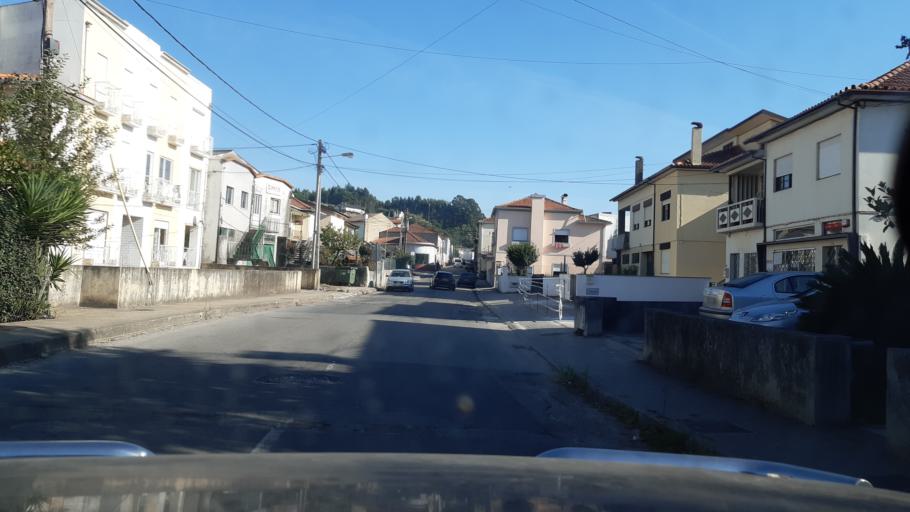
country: PT
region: Aveiro
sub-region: Agueda
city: Agueda
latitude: 40.5727
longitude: -8.4357
